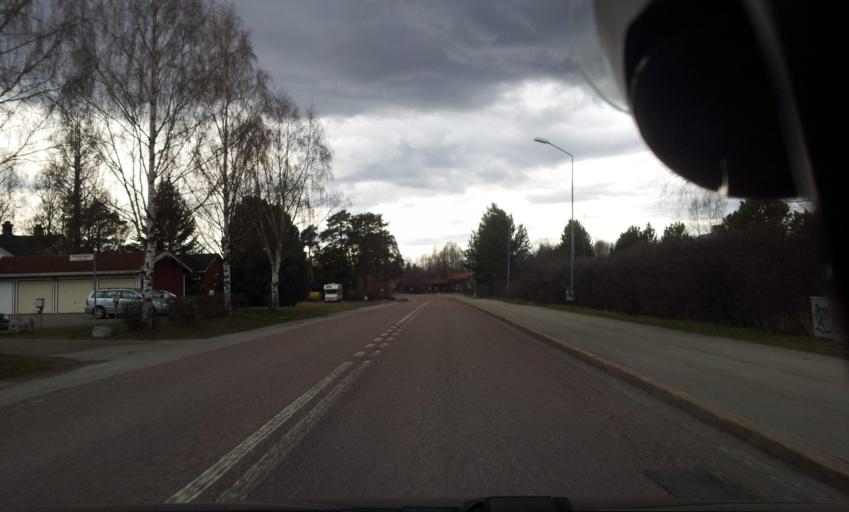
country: SE
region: Gaevleborg
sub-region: Ljusdals Kommun
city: Ljusdal
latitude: 61.8358
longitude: 16.0650
